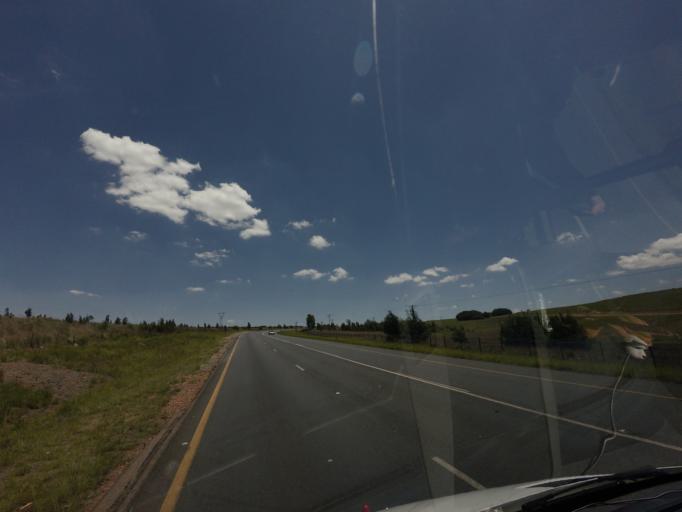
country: ZA
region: Mpumalanga
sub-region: Nkangala District Municipality
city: Belfast
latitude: -25.7236
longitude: 30.1443
